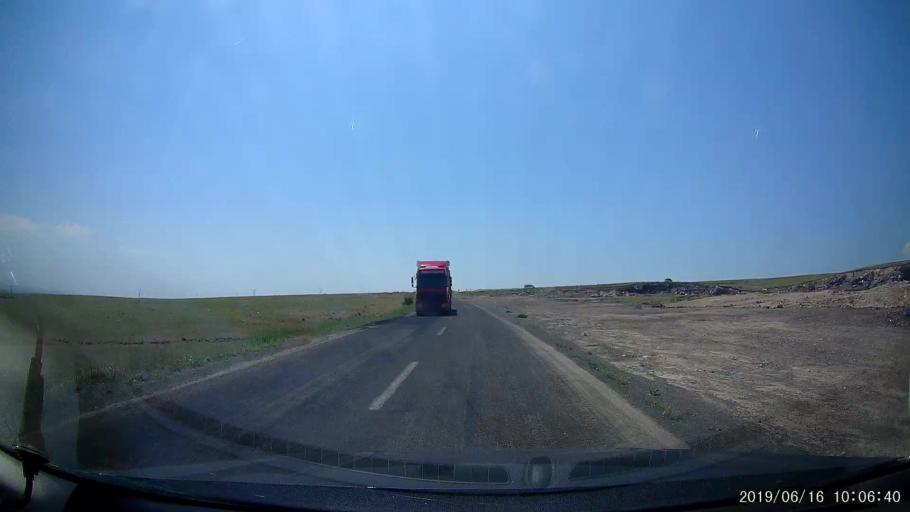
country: TR
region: Kars
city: Digor
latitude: 40.2523
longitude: 43.5450
